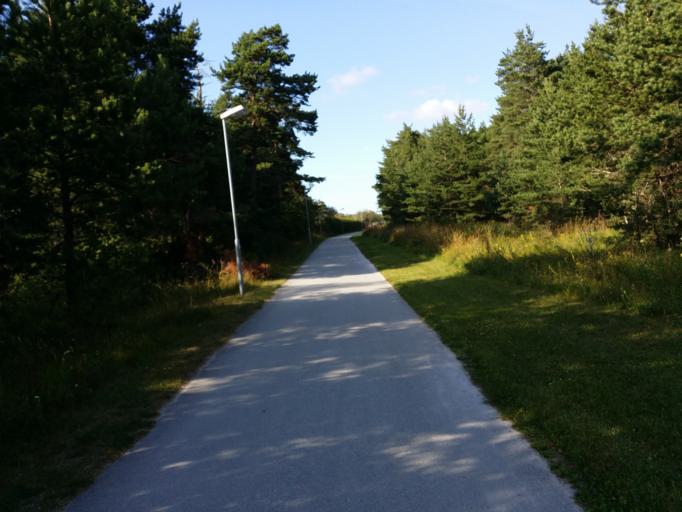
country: SE
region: Gotland
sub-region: Gotland
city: Visby
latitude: 57.6286
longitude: 18.3231
